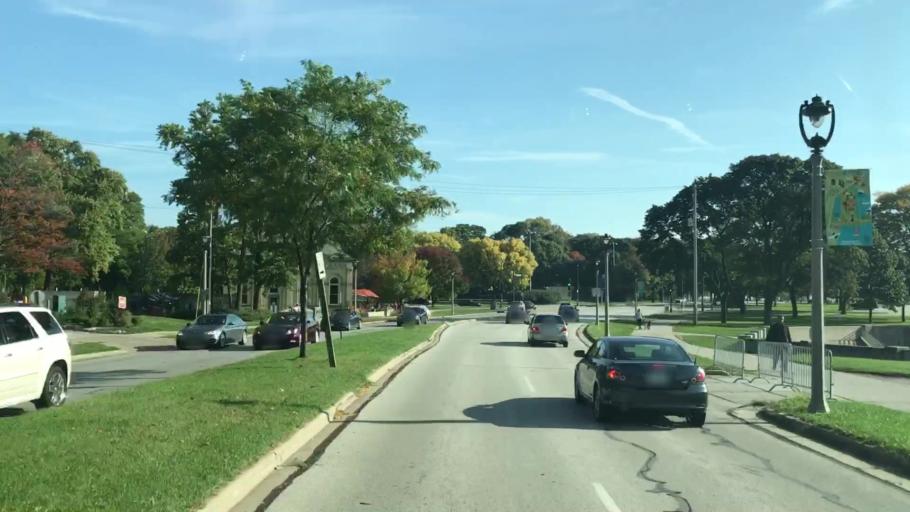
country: US
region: Wisconsin
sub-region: Milwaukee County
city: Milwaukee
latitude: 43.0529
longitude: -87.8876
